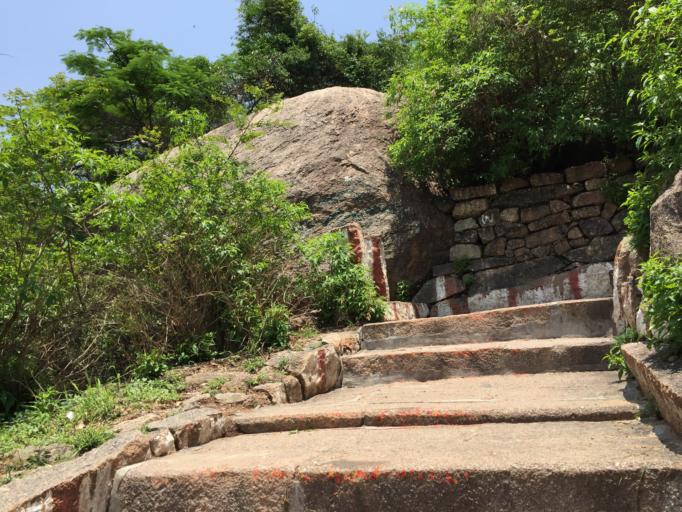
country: IN
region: Karnataka
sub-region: Mysore
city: Mysore
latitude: 12.2829
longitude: 76.6673
